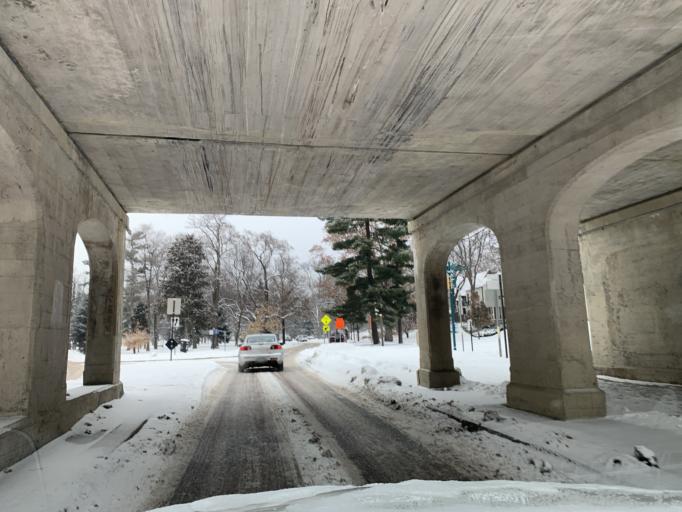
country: US
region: Minnesota
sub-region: Hennepin County
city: Saint Louis Park
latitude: 44.9509
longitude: -93.3166
